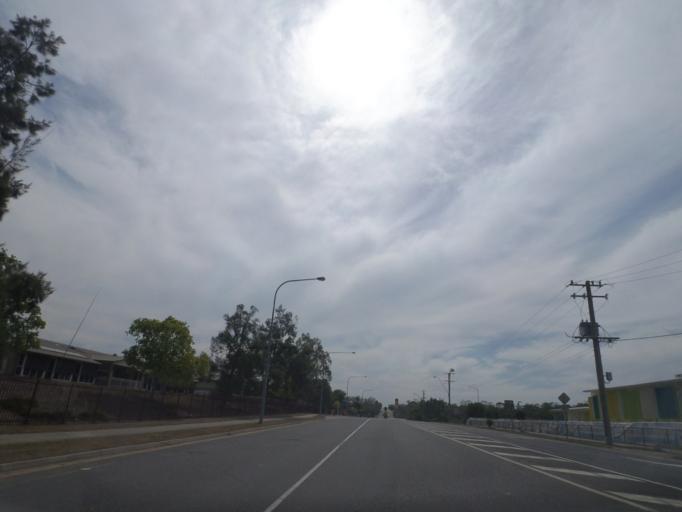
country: AU
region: Queensland
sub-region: Brisbane
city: Sunnybank Hills
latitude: -27.6402
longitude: 153.0567
